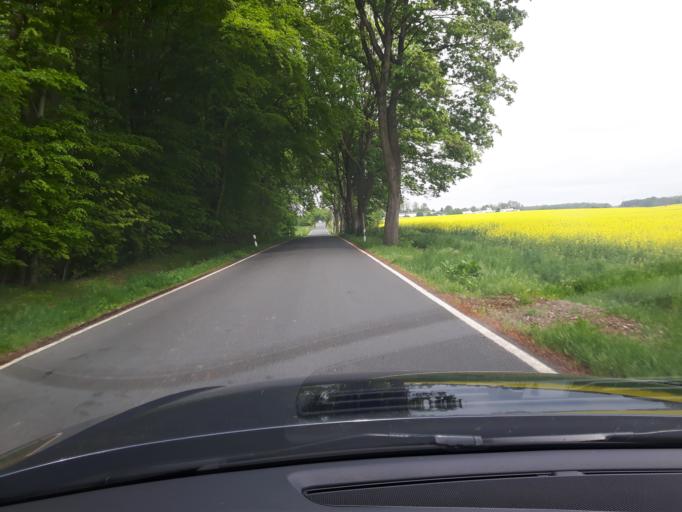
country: DE
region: Mecklenburg-Vorpommern
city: Tribsees
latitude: 54.1829
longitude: 12.7401
